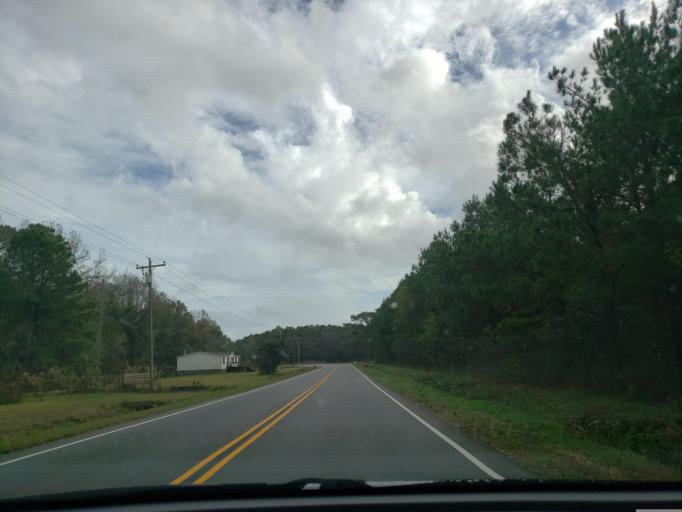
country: US
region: North Carolina
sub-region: Duplin County
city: Beulaville
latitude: 34.8326
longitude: -77.8522
